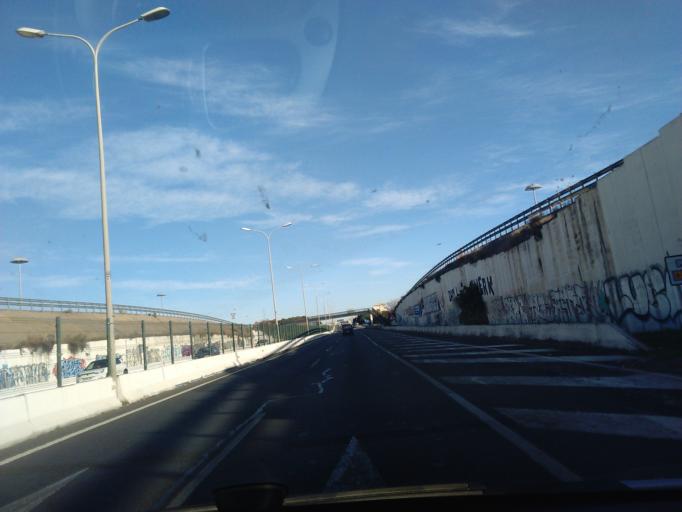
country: ES
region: Andalusia
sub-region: Provincia de Sevilla
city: Sevilla
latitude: 37.3863
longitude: -5.9392
